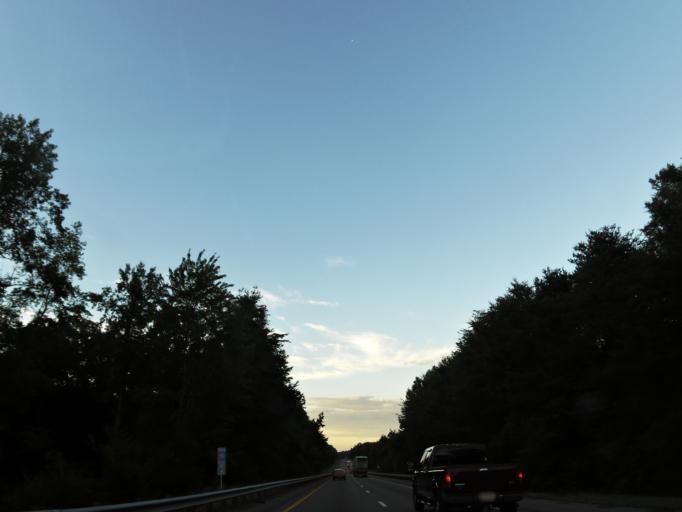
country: US
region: Tennessee
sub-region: McMinn County
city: Athens
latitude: 35.3983
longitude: -84.7122
